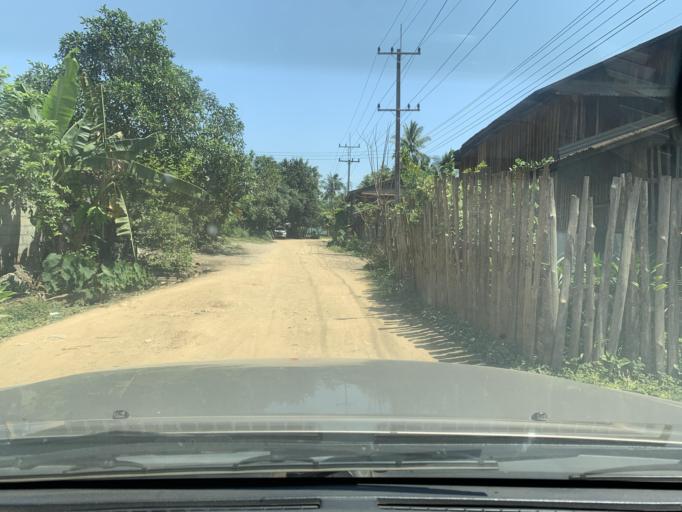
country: LA
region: Louangphabang
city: Louangphabang
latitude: 19.9053
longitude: 102.2279
